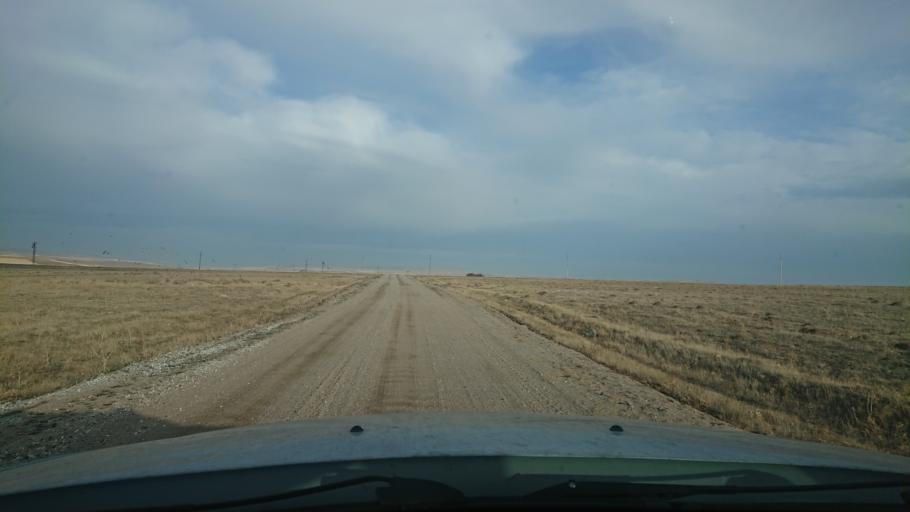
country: TR
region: Aksaray
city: Agacoren
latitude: 38.7170
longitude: 33.8685
